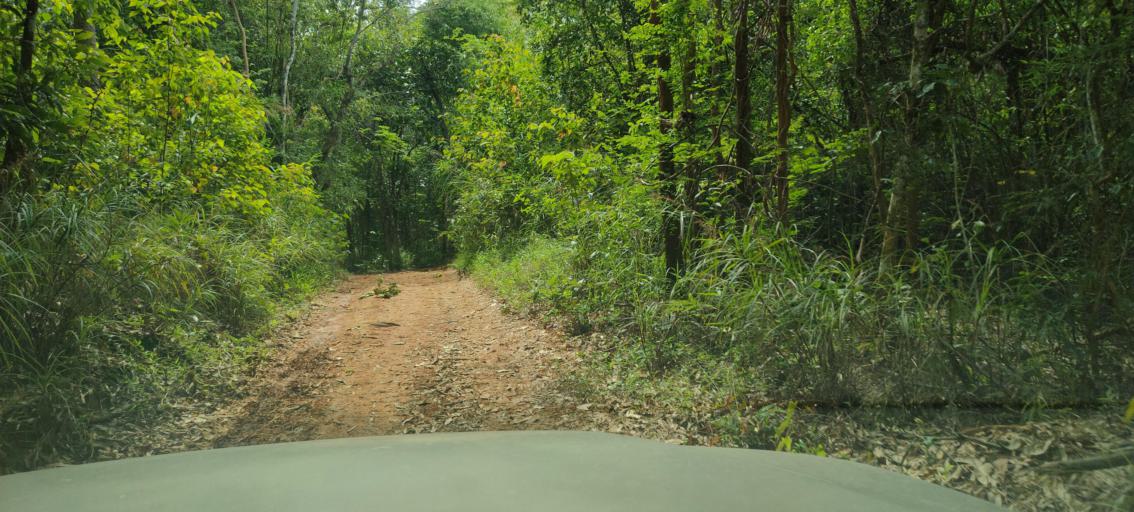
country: LA
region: Loungnamtha
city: Muang Nale
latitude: 20.4139
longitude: 101.4783
